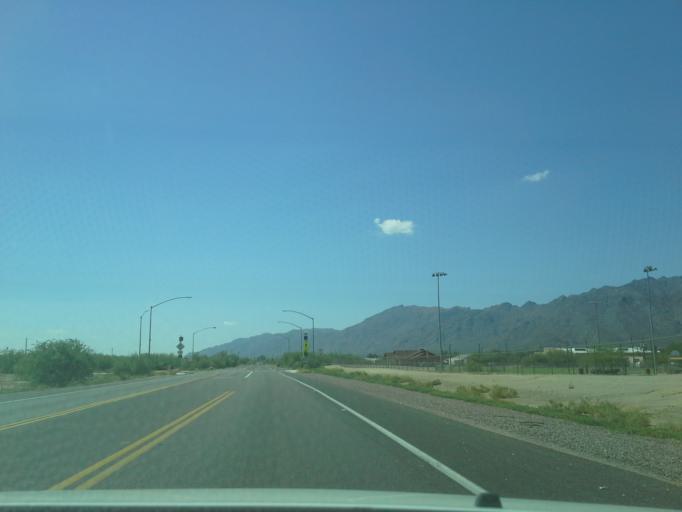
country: US
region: Arizona
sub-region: Maricopa County
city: Laveen
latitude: 33.2968
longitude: -112.1691
